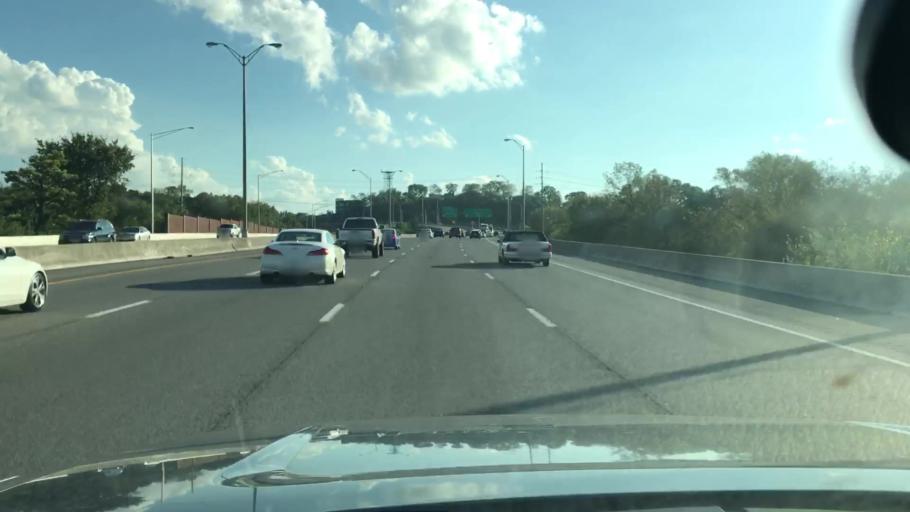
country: US
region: Tennessee
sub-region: Davidson County
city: Nashville
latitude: 36.1611
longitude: -86.8211
